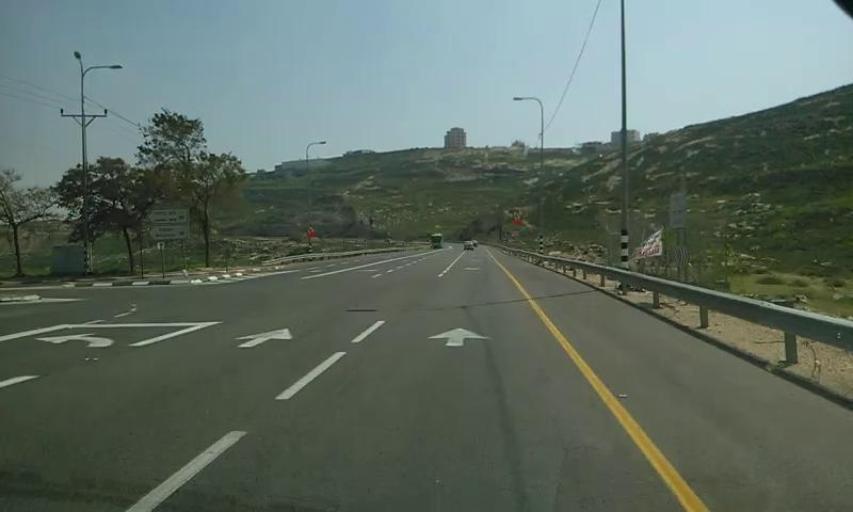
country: PS
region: West Bank
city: Jaba`
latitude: 31.8640
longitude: 35.2596
